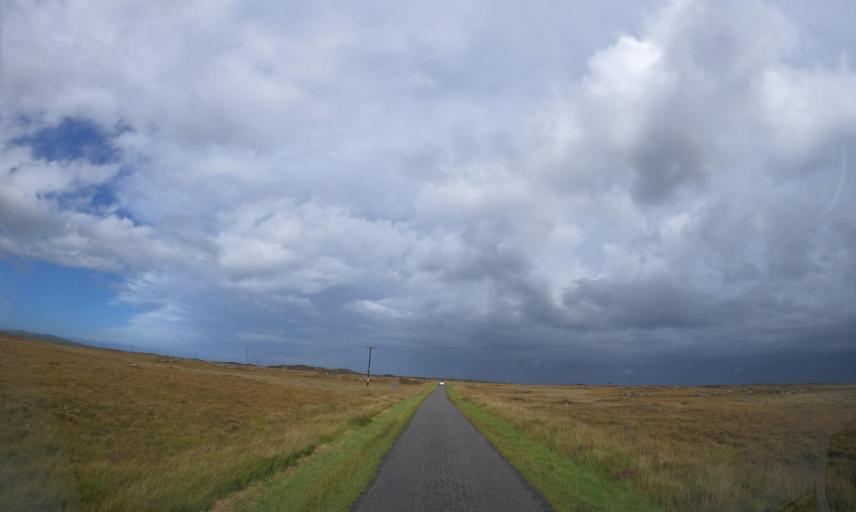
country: GB
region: Scotland
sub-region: Eilean Siar
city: Barra
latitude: 56.5153
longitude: -6.8331
